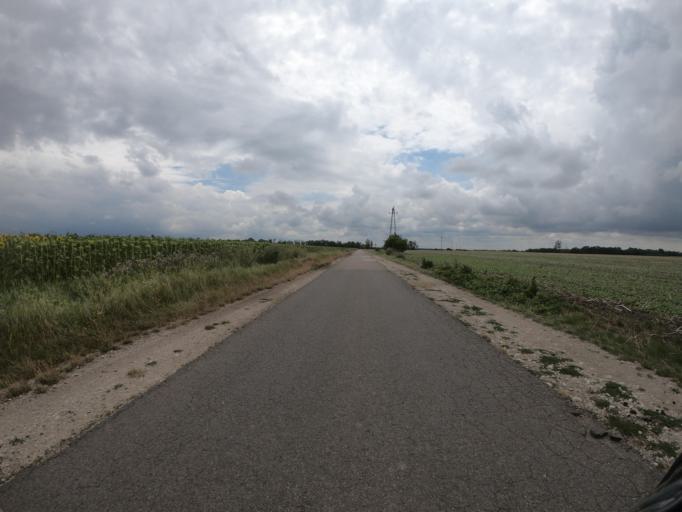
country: HU
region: Borsod-Abauj-Zemplen
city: Szentistvan
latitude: 47.7447
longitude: 20.6800
